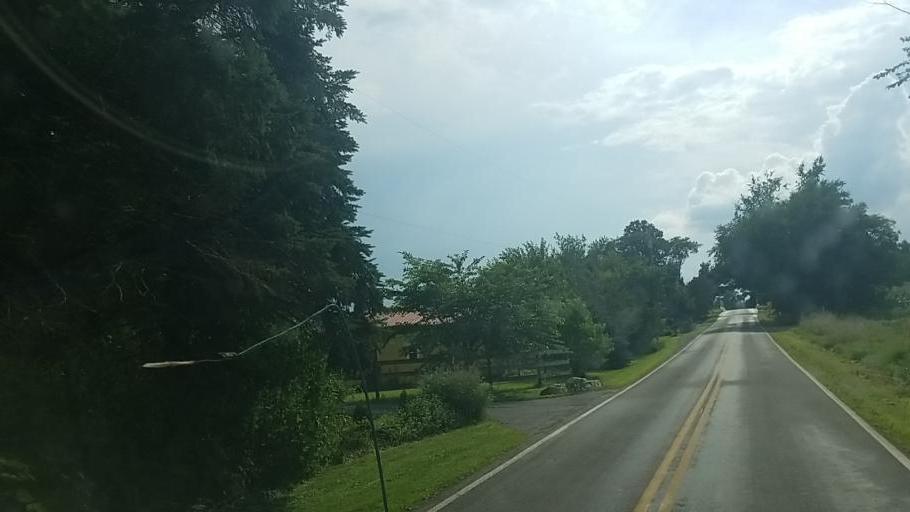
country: US
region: Ohio
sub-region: Medina County
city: Westfield Center
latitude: 40.9980
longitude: -81.9247
